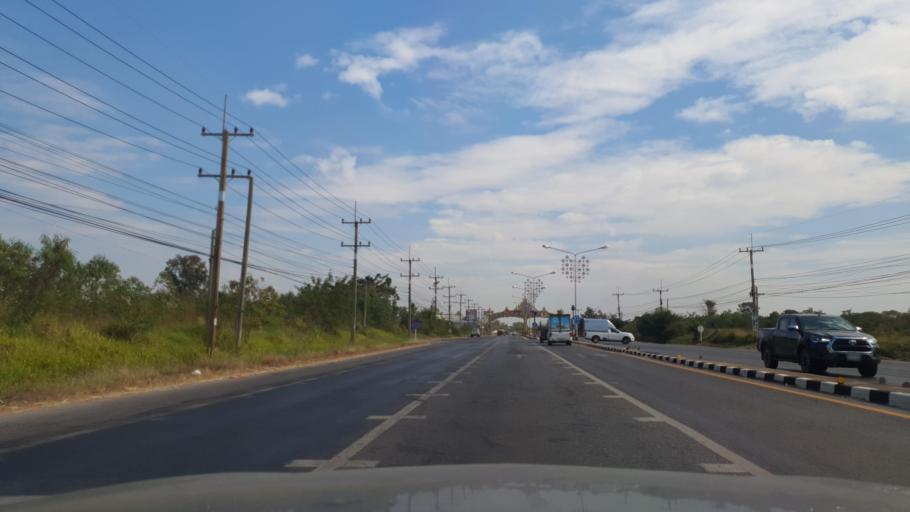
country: TH
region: Kalasin
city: Kalasin
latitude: 16.4061
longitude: 103.4446
